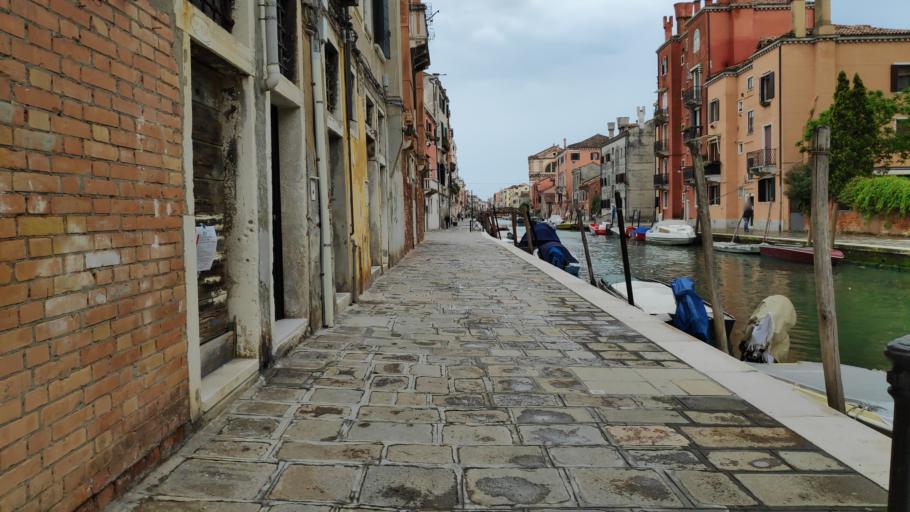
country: IT
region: Veneto
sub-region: Provincia di Venezia
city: Venice
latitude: 45.4469
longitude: 12.3226
